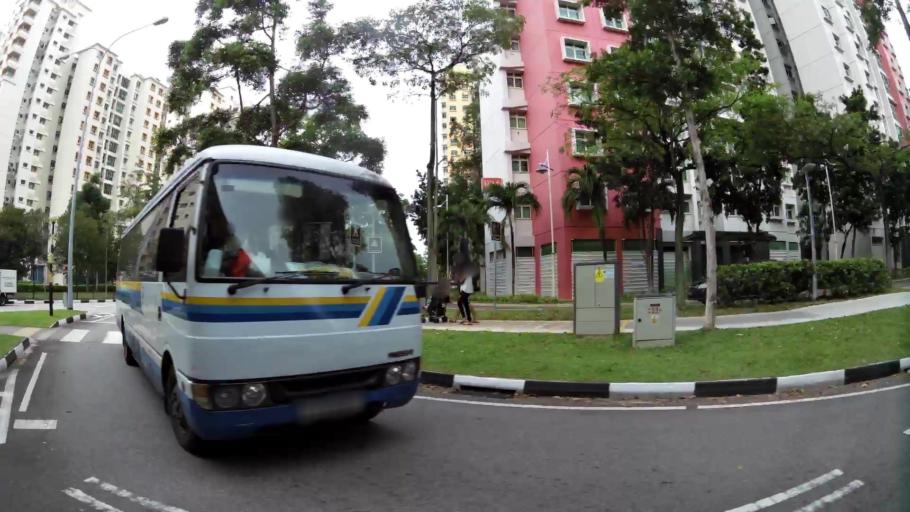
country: MY
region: Johor
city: Kampung Pasir Gudang Baru
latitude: 1.3953
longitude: 103.9112
